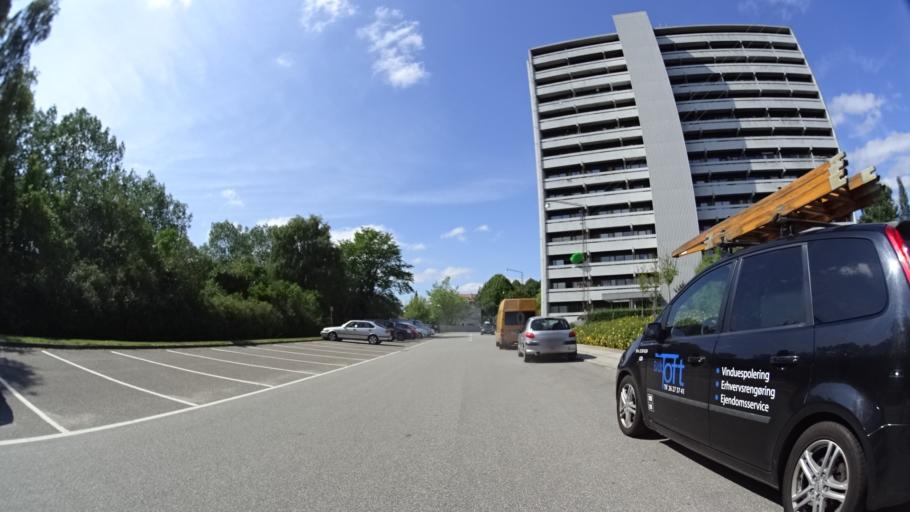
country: DK
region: Central Jutland
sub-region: Arhus Kommune
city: Arhus
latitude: 56.1410
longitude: 10.1977
